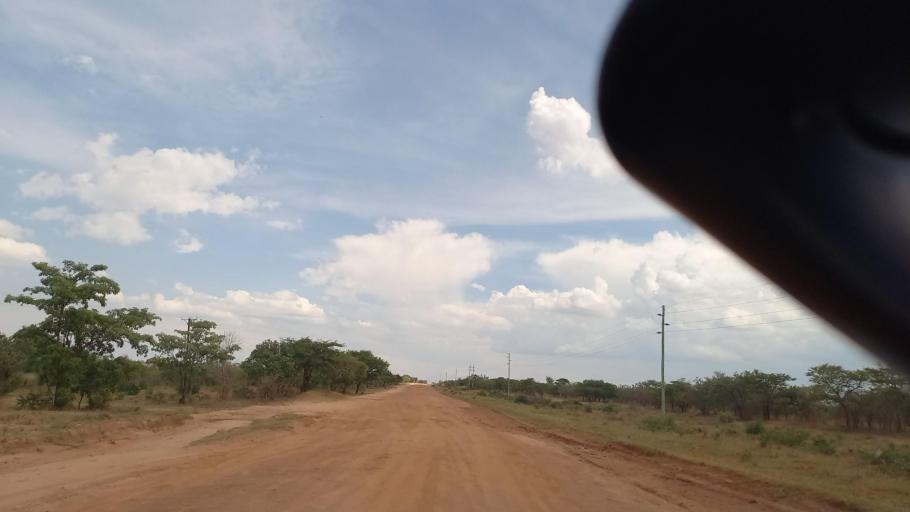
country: ZM
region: Lusaka
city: Kafue
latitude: -16.1405
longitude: 28.0530
